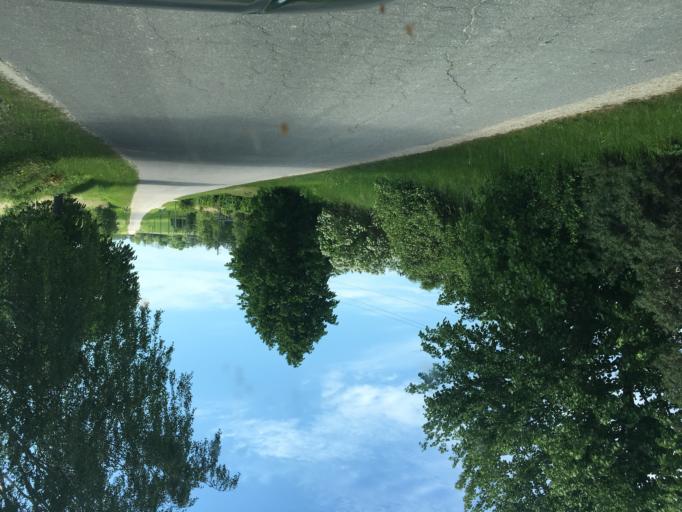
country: LV
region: Talsu Rajons
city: Valdemarpils
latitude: 57.3761
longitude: 22.6037
